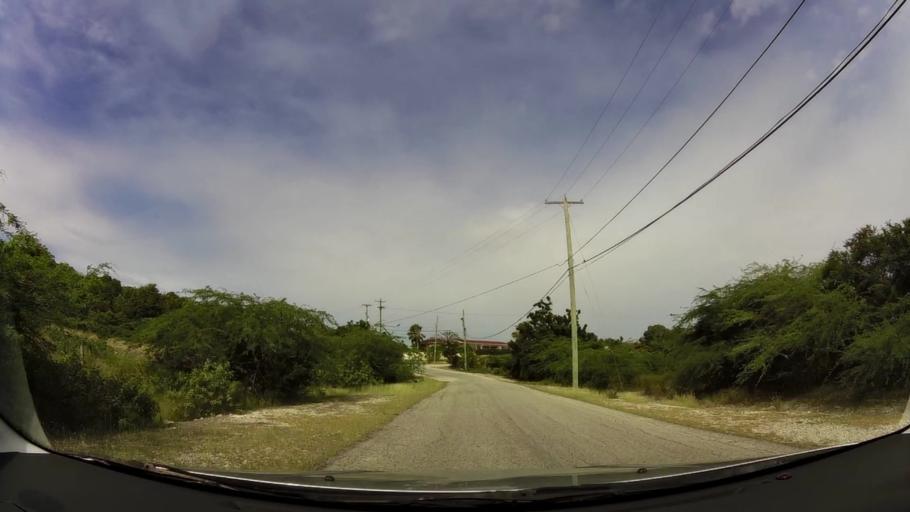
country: AG
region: Saint Paul
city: Falmouth
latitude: 17.0412
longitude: -61.7040
